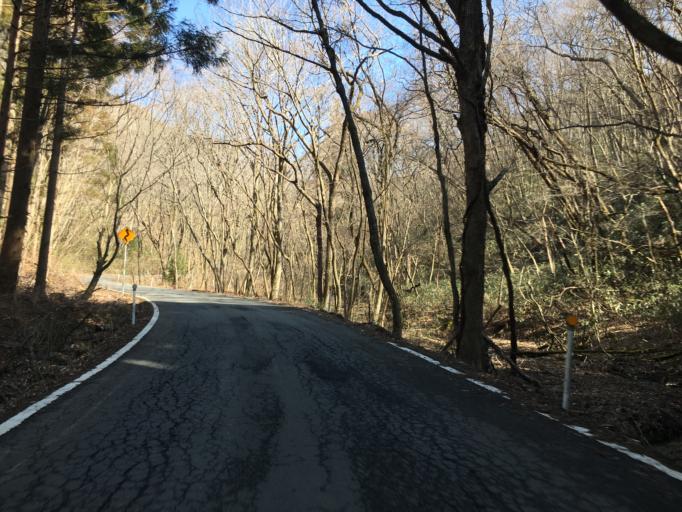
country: JP
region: Ibaraki
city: Takahagi
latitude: 36.8316
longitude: 140.5556
